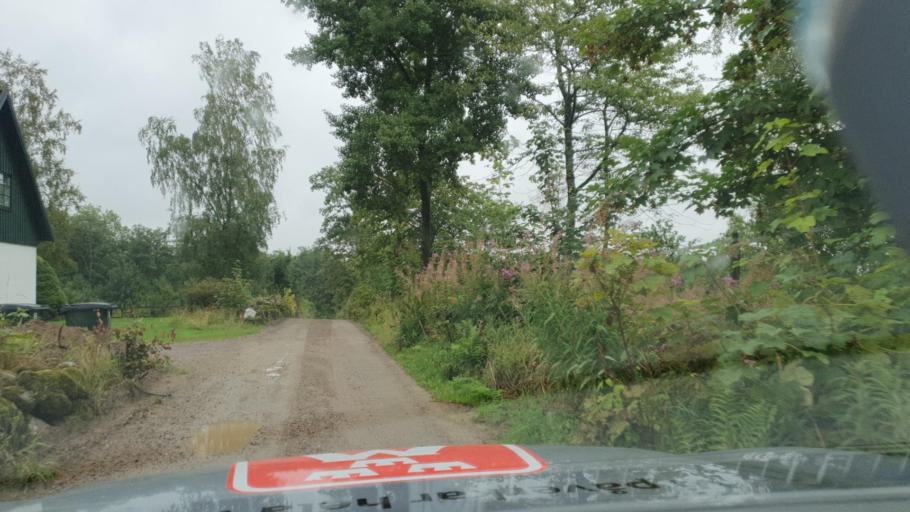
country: SE
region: Skane
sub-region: Kristianstads Kommun
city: Degeberga
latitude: 55.7712
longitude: 13.9192
